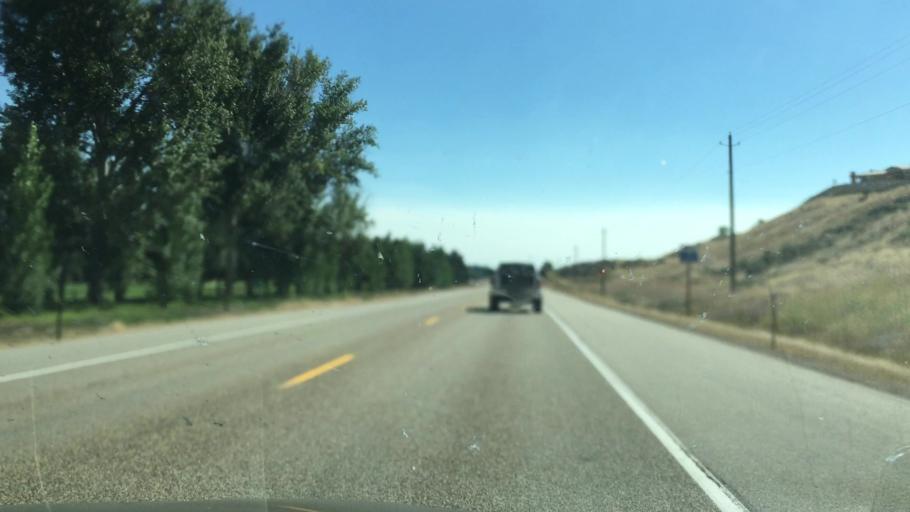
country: US
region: Idaho
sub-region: Ada County
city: Eagle
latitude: 43.7421
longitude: -116.3005
